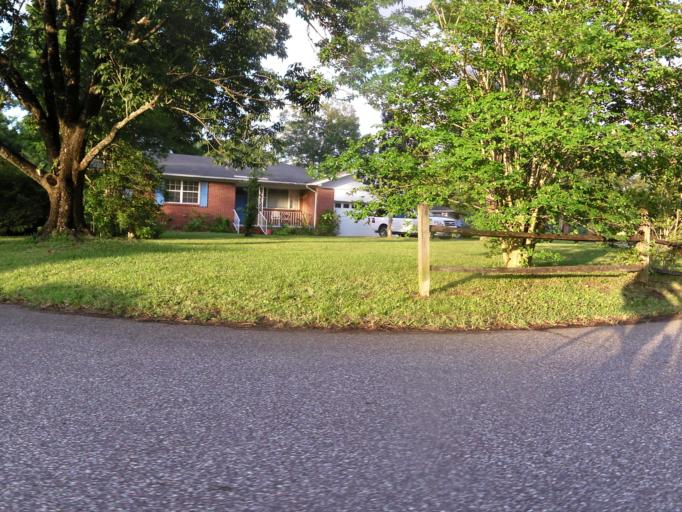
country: US
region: Florida
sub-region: Clay County
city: Orange Park
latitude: 30.2266
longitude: -81.6082
